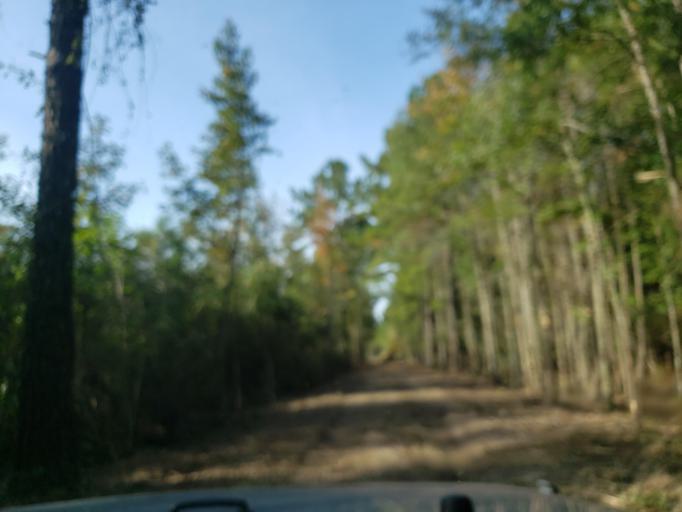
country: US
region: Georgia
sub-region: Chatham County
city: Georgetown
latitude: 32.0426
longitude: -81.2403
